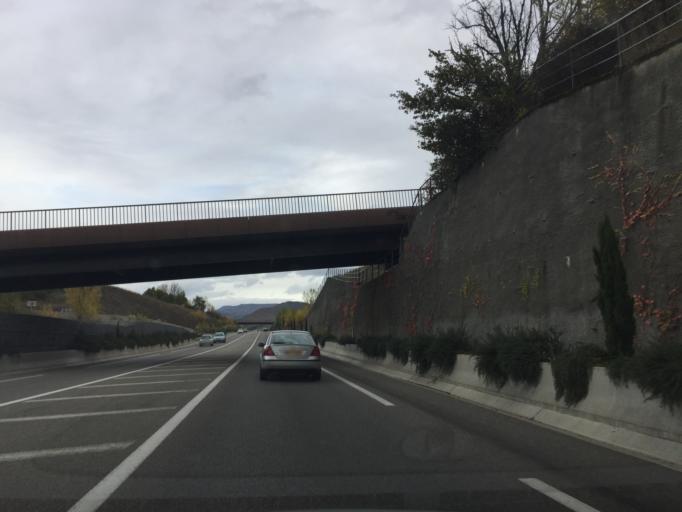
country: FR
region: Rhone-Alpes
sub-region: Departement de l'Ardeche
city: Saint-Etienne-de-Fontbellon
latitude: 44.6052
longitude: 4.4005
